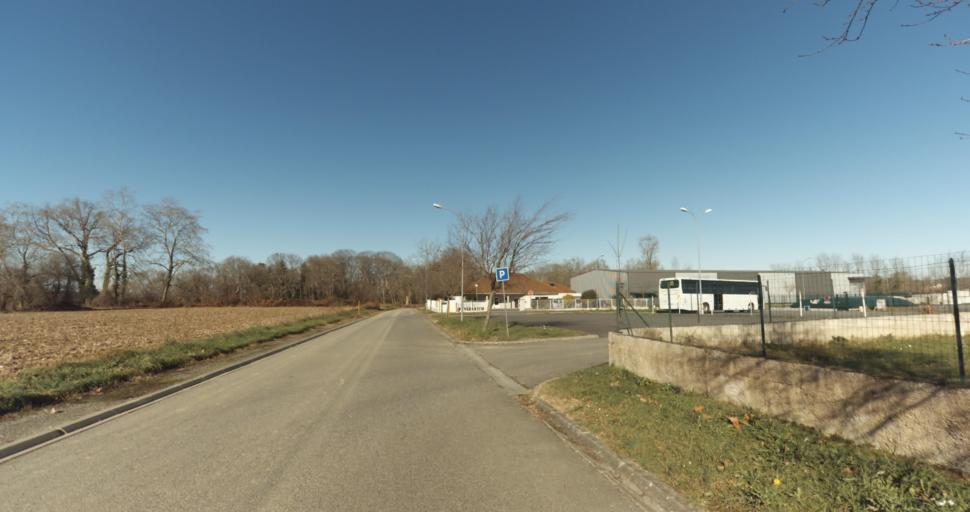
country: FR
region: Aquitaine
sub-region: Departement des Pyrenees-Atlantiques
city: Morlaas
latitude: 43.3532
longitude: -0.2585
